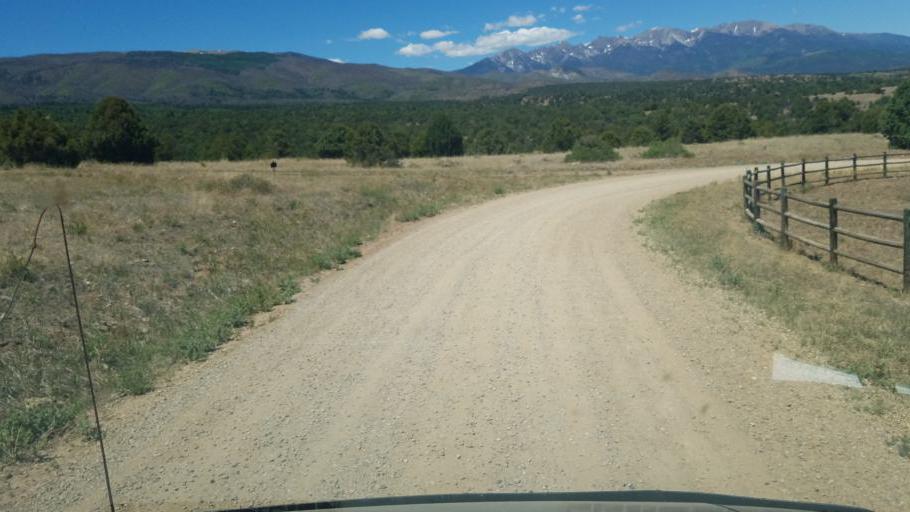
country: US
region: Colorado
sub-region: Custer County
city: Westcliffe
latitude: 38.3053
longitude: -105.6772
